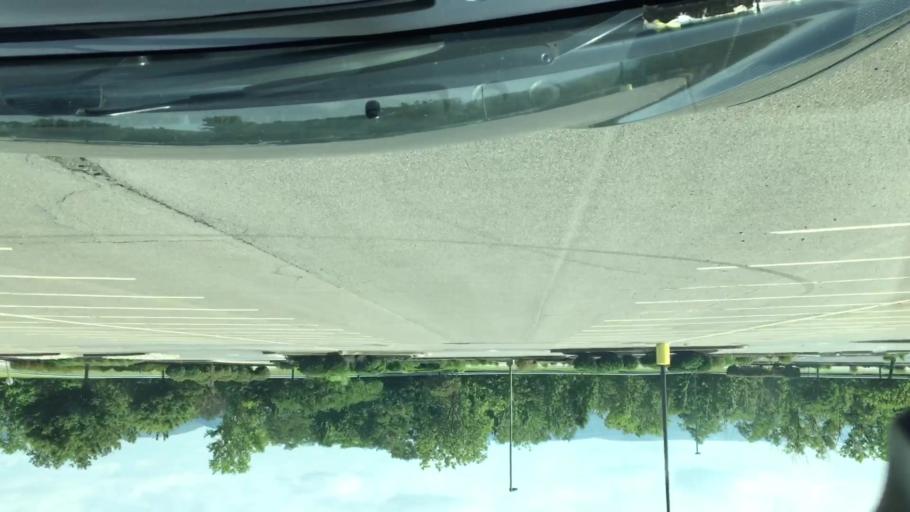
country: US
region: Pennsylvania
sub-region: Luzerne County
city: Georgetown
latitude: 41.2462
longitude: -75.8471
